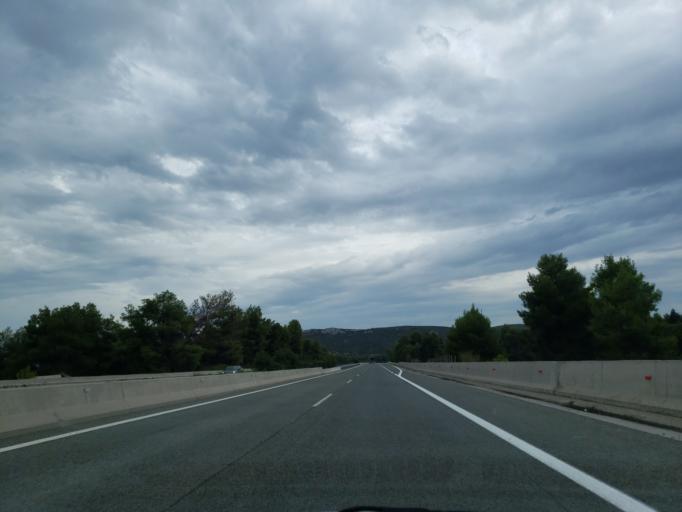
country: GR
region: Central Greece
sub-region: Nomos Voiotias
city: Akraifnia
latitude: 38.4066
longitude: 23.2184
